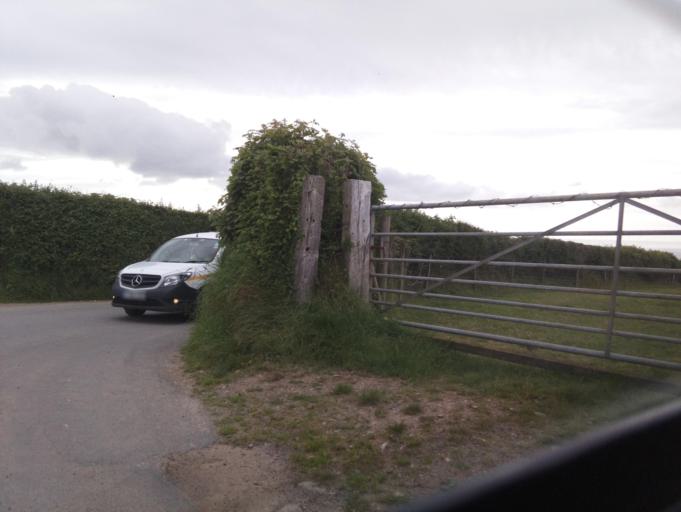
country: GB
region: England
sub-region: Devon
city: Dartmouth
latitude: 50.3198
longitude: -3.6287
